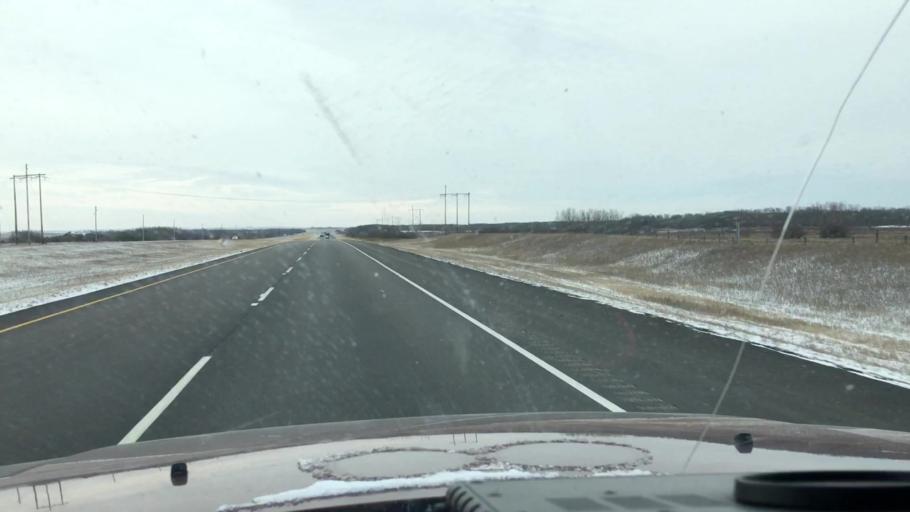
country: CA
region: Saskatchewan
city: Saskatoon
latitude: 51.8936
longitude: -106.5184
